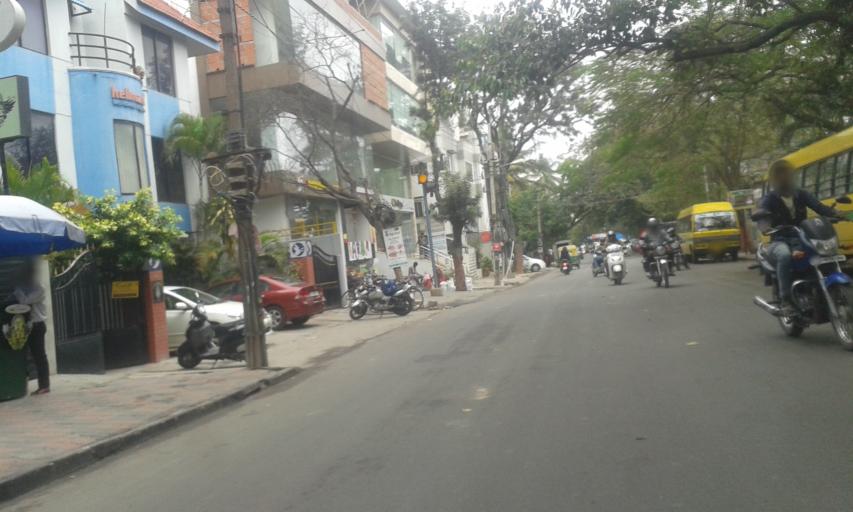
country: IN
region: Karnataka
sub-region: Bangalore Urban
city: Bangalore
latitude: 12.9703
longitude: 77.6452
